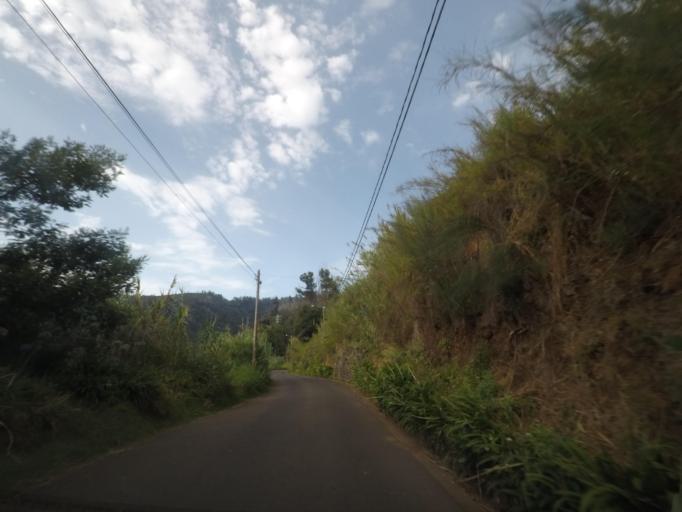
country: PT
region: Madeira
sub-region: Calheta
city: Arco da Calheta
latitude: 32.7349
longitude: -17.1540
